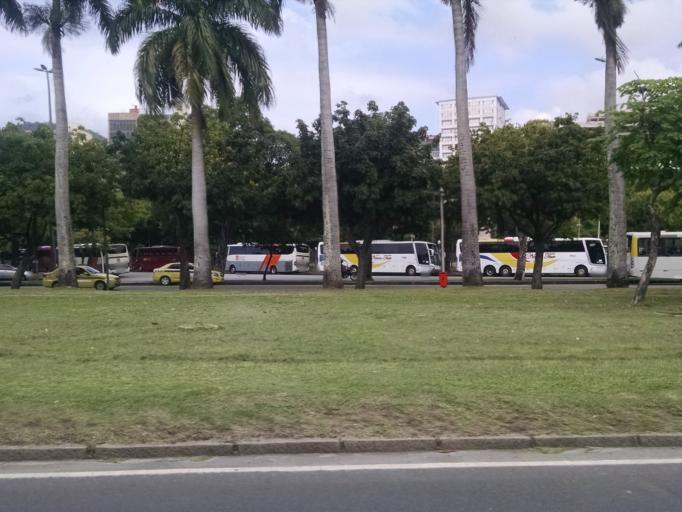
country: BR
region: Rio de Janeiro
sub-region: Rio De Janeiro
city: Rio de Janeiro
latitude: -22.9183
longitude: -43.1748
